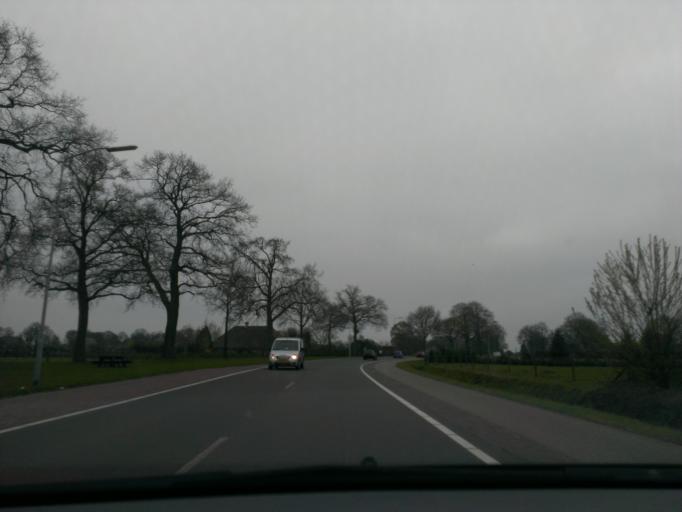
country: NL
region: Gelderland
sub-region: Gemeente Epe
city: Emst
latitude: 52.3281
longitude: 5.9814
